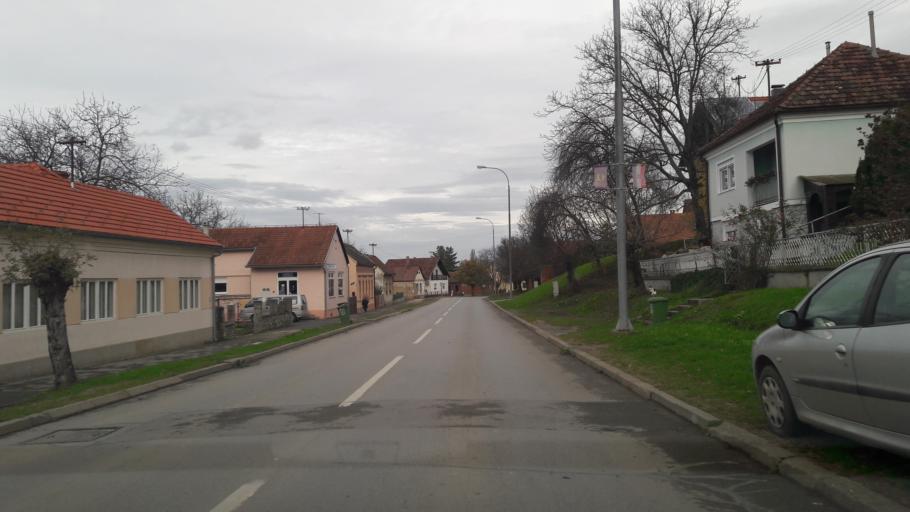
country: HR
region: Virovitick-Podravska
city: Orahovica
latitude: 45.5340
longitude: 17.8876
